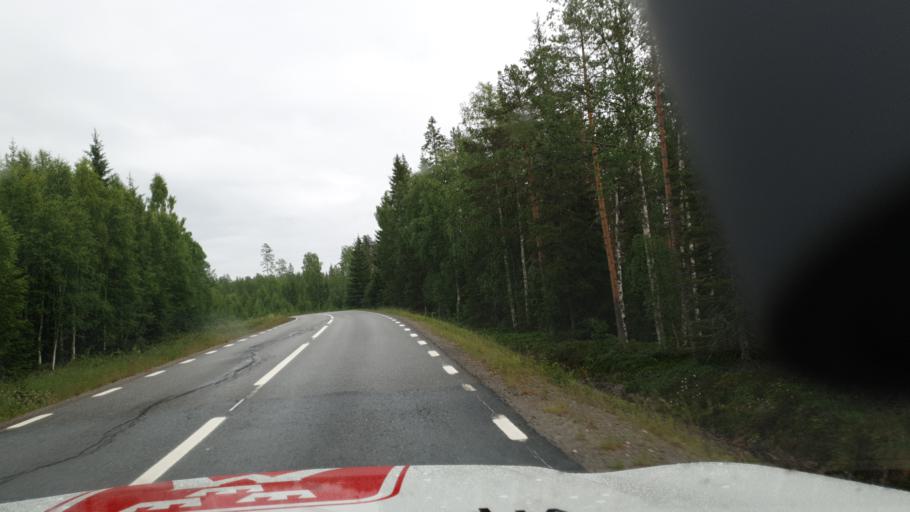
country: SE
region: Vaesterbotten
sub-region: Vannas Kommun
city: Vannasby
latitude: 63.8498
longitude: 19.9632
